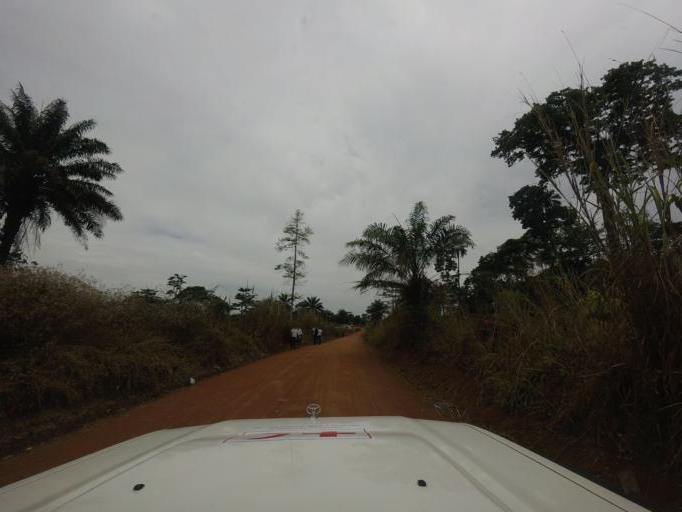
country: SL
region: Eastern Province
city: Buedu
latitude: 8.3445
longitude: -10.2057
